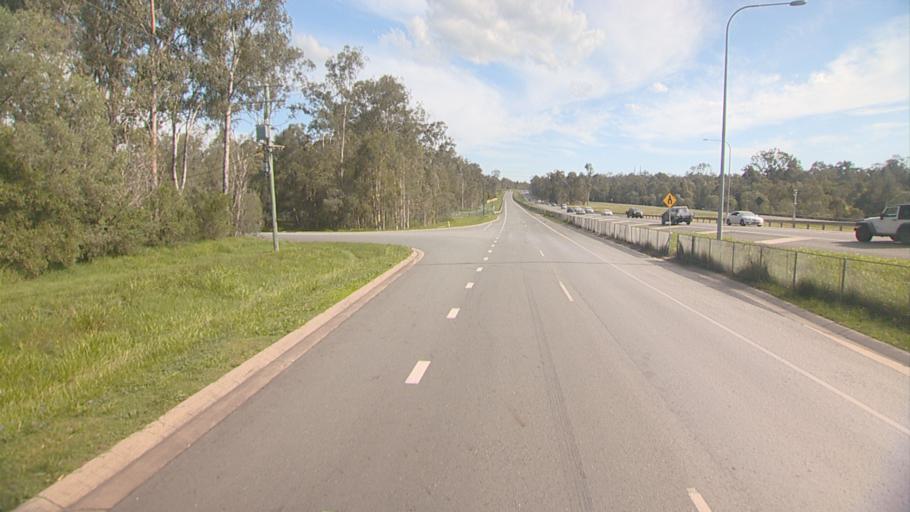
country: AU
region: Queensland
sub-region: Logan
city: Park Ridge South
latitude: -27.7289
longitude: 153.0296
